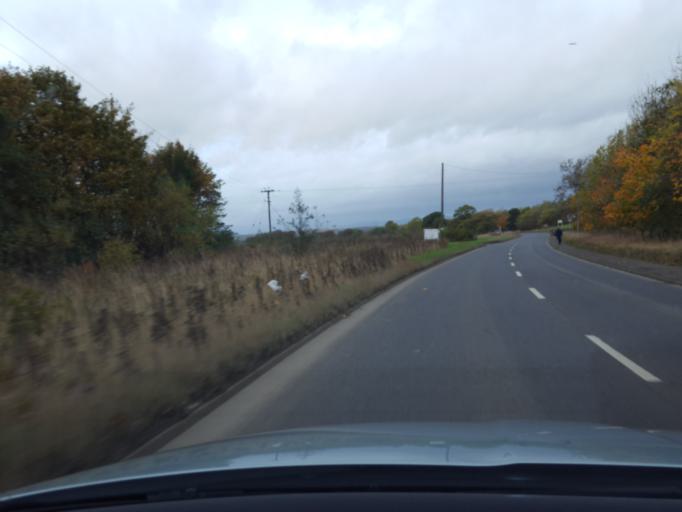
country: GB
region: Scotland
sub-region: Edinburgh
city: Newbridge
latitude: 55.9153
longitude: -3.4086
